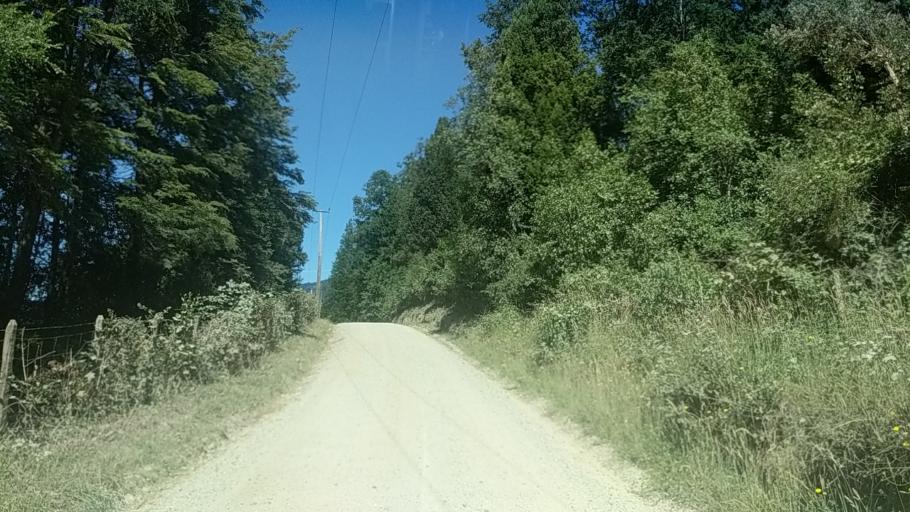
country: CL
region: Araucania
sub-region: Provincia de Cautin
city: Pucon
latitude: -39.0637
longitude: -71.7326
